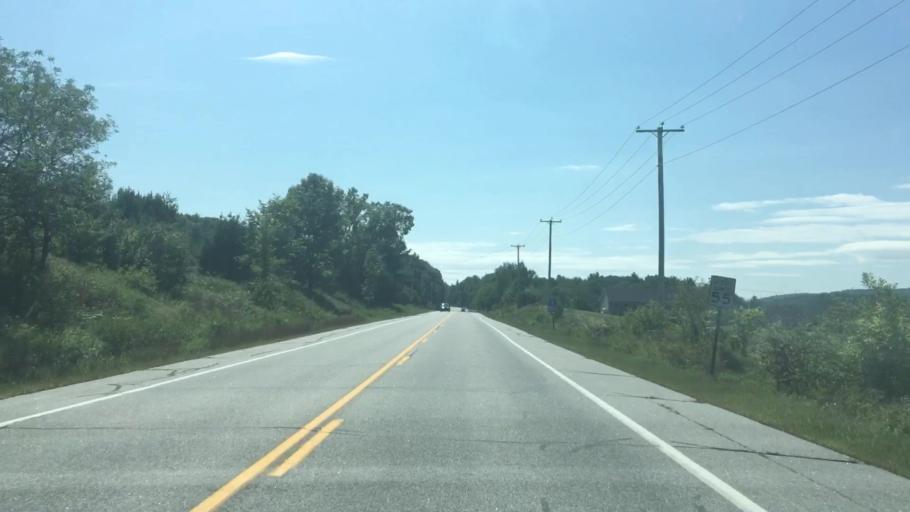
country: US
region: Maine
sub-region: Kennebec County
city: Monmouth
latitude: 44.1637
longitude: -70.0295
